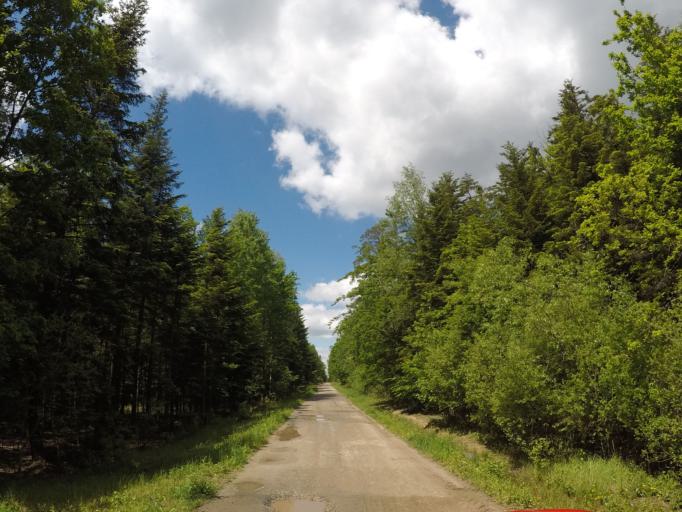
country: PL
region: Swietokrzyskie
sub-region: Powiat kielecki
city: Domaszowice
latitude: 50.9126
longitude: 20.6546
